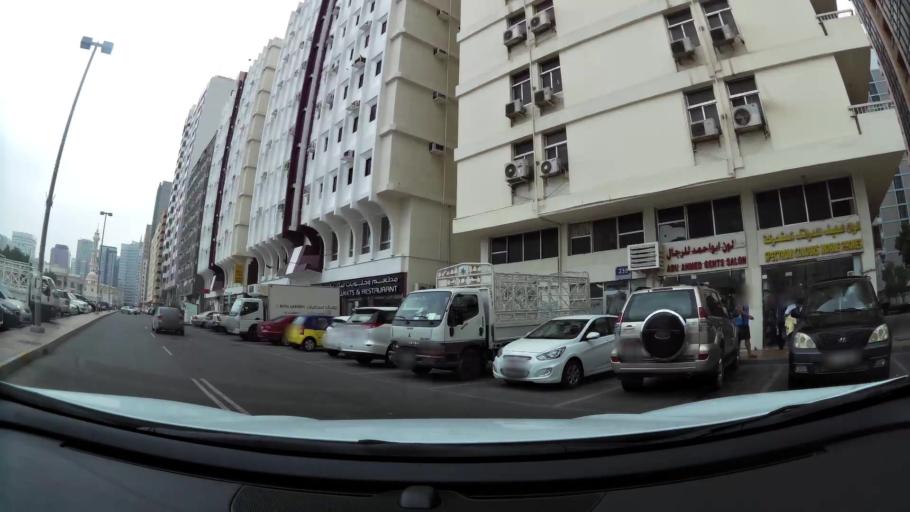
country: AE
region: Abu Dhabi
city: Abu Dhabi
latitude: 24.4802
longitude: 54.3703
